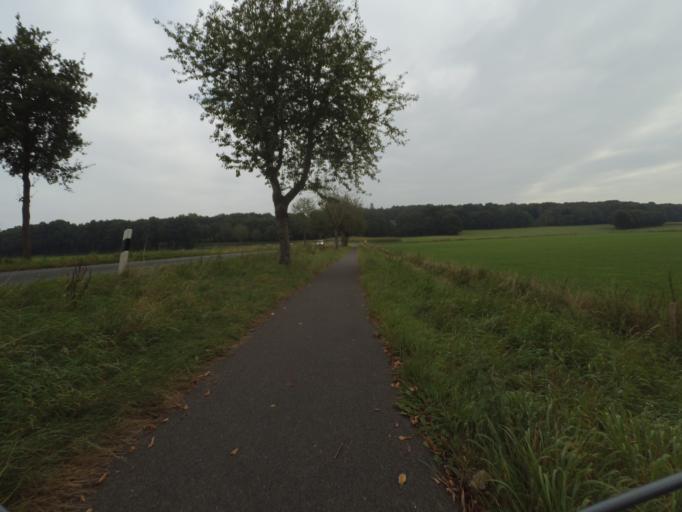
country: DE
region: Lower Saxony
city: Bad Bentheim
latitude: 52.2923
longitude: 7.0901
